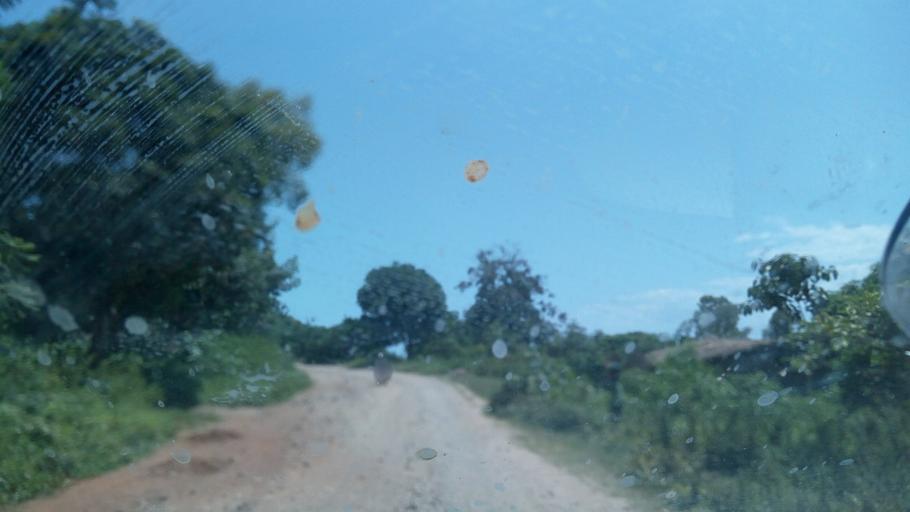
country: CD
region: South Kivu
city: Uvira
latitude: -3.4937
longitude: 29.1381
